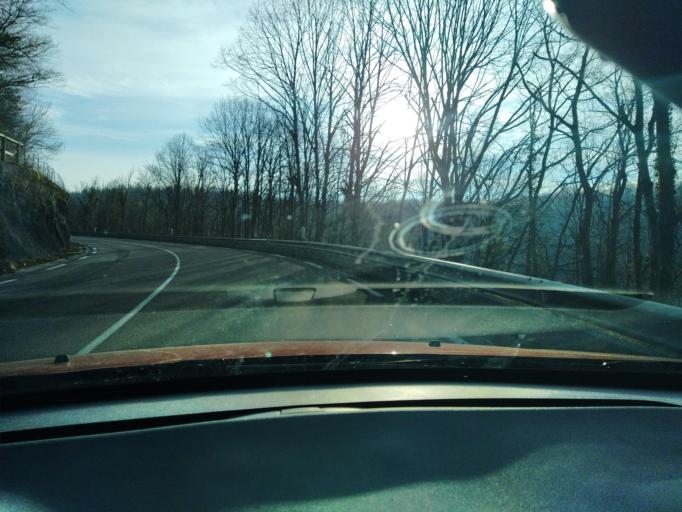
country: FR
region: Franche-Comte
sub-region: Departement du Jura
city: Perrigny
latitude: 46.6248
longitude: 5.6114
